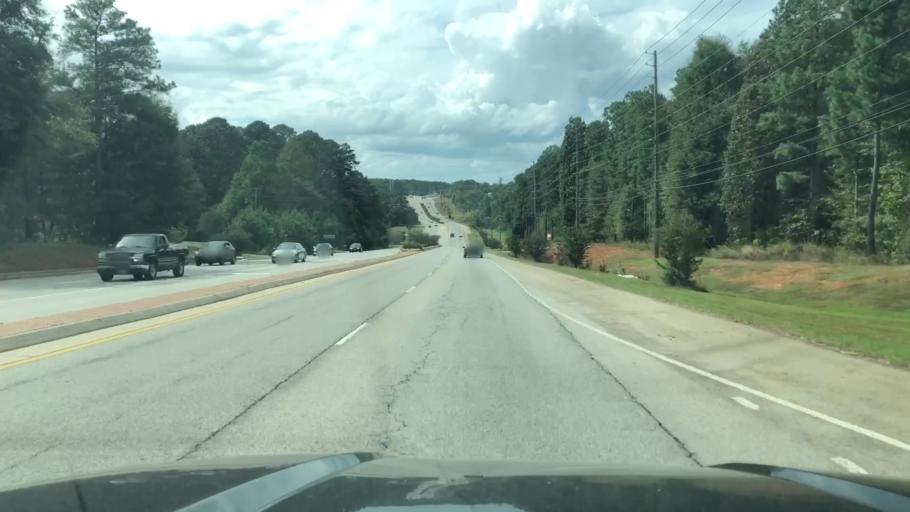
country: US
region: Georgia
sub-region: Henry County
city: McDonough
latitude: 33.4593
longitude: -84.1817
